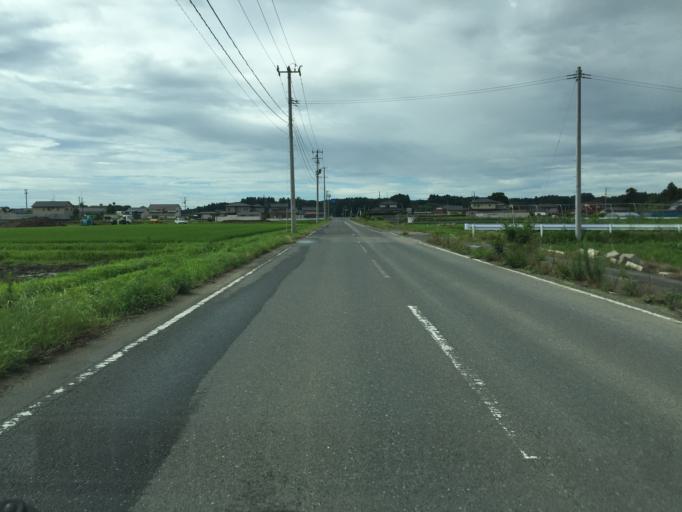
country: JP
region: Miyagi
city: Marumori
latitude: 37.7894
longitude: 140.9571
